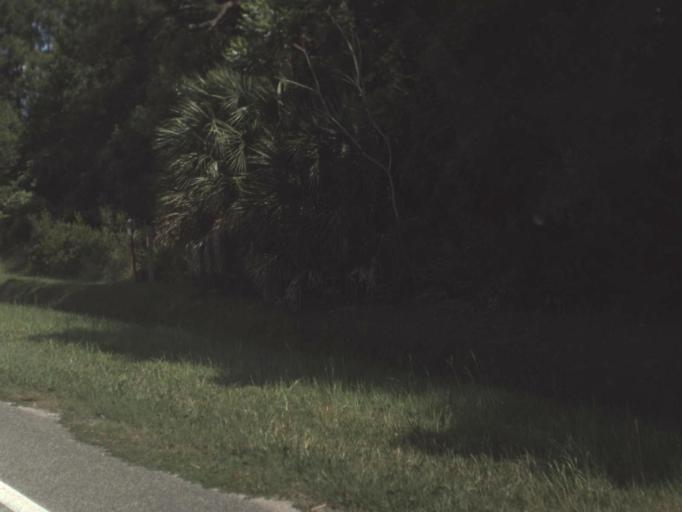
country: US
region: Florida
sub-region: Putnam County
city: Palatka
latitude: 29.6623
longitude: -81.6805
